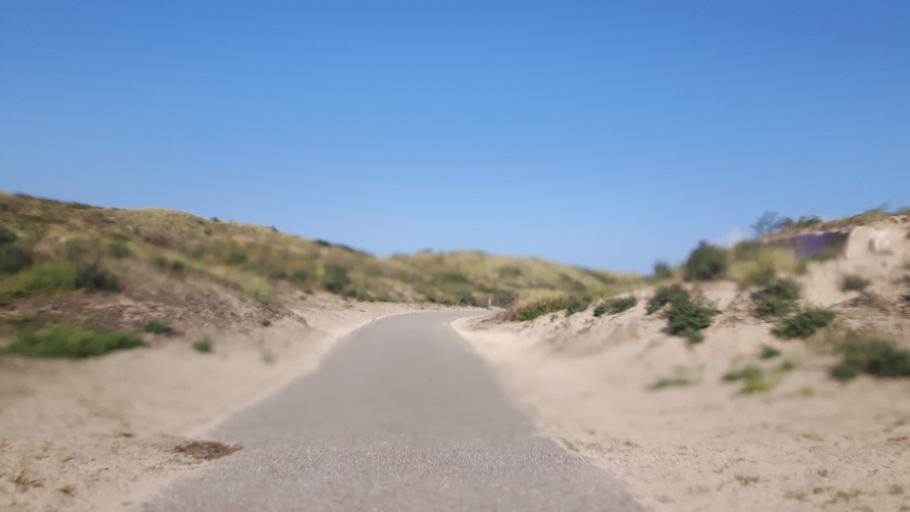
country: NL
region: North Holland
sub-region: Gemeente Zandvoort
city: Zandvoort
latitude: 52.3943
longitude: 4.5506
